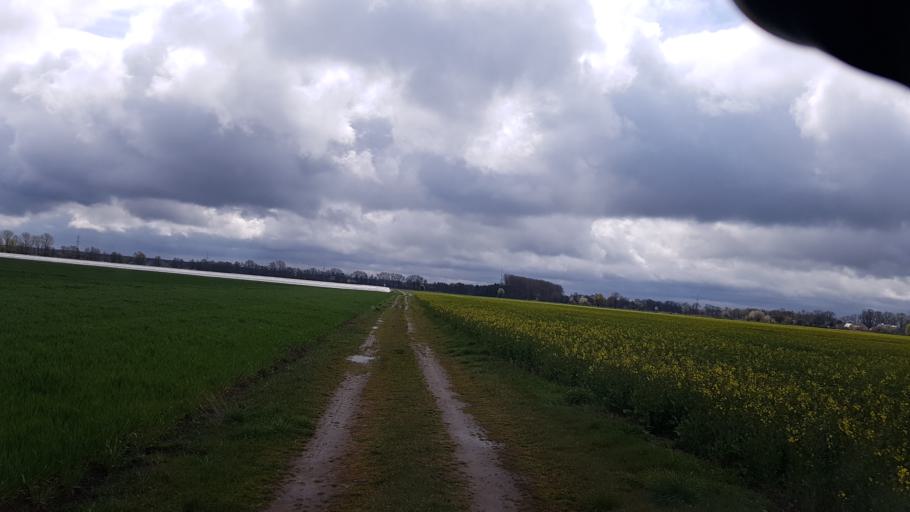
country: DE
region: Brandenburg
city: Doberlug-Kirchhain
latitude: 51.6590
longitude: 13.5512
